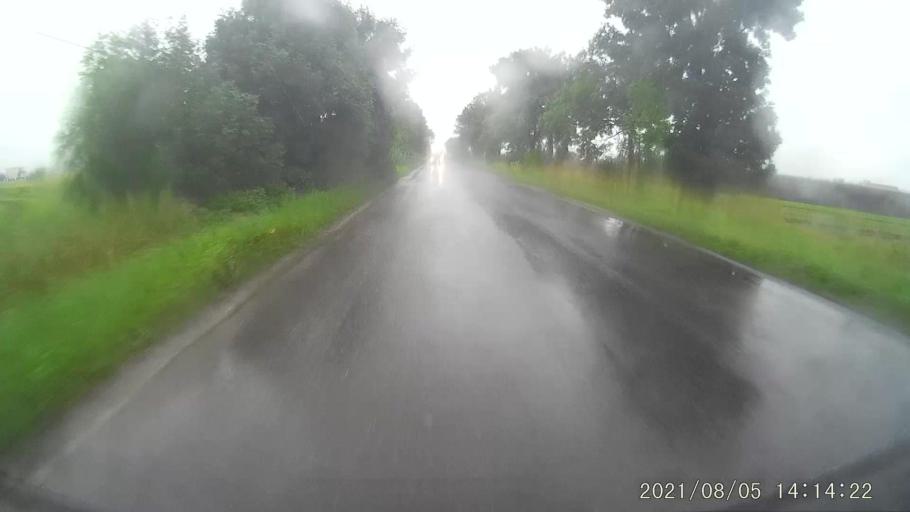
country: PL
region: Opole Voivodeship
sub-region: Powiat prudnicki
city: Biala
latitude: 50.4685
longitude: 17.7410
